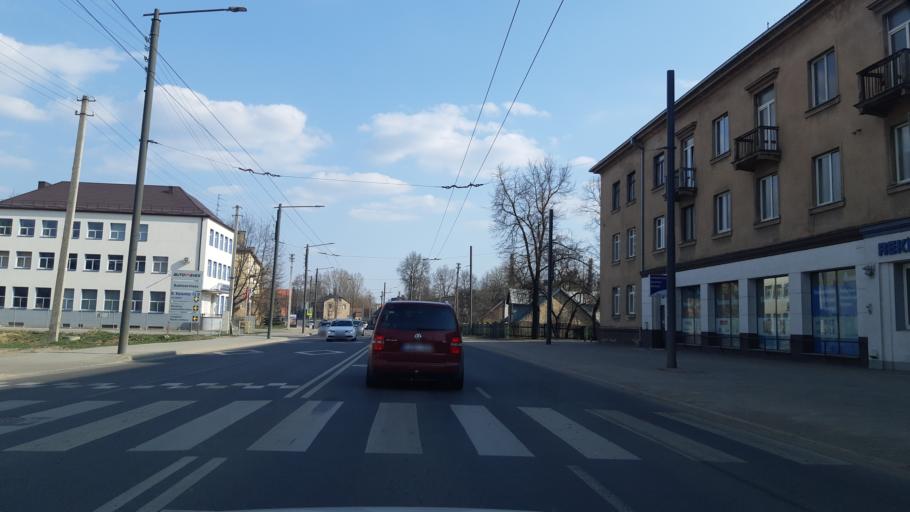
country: LT
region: Kauno apskritis
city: Dainava (Kaunas)
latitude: 54.8961
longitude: 23.9811
